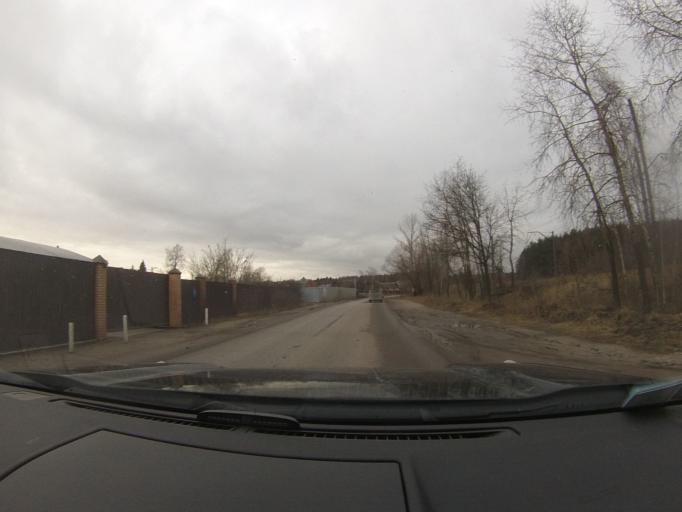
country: RU
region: Moskovskaya
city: Voskresensk
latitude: 55.3296
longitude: 38.6799
